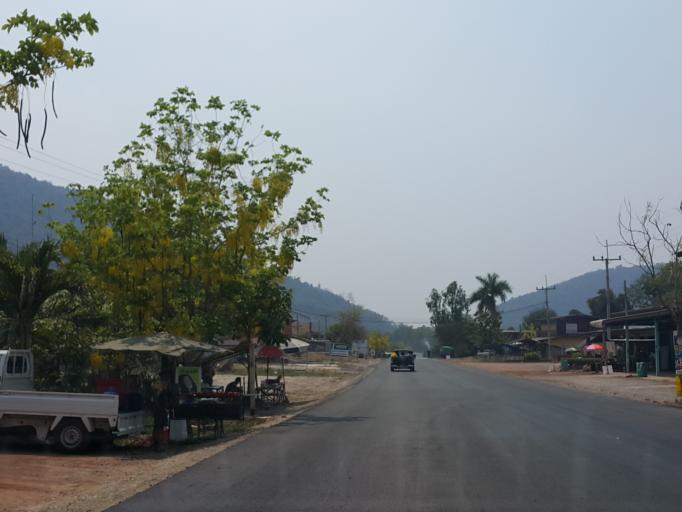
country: TH
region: Nakhon Sawan
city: Mae Wong
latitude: 15.8990
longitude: 99.4679
